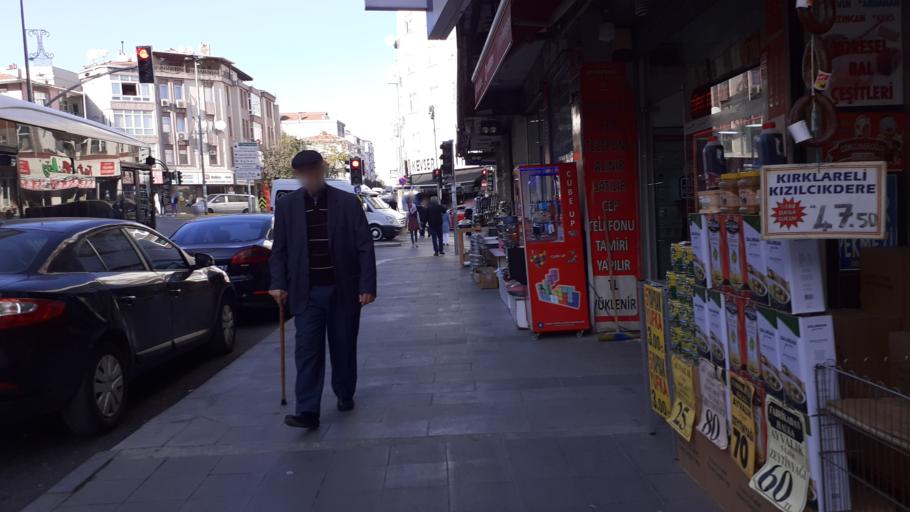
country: TR
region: Istanbul
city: Mahmutbey
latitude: 41.0092
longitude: 28.7988
